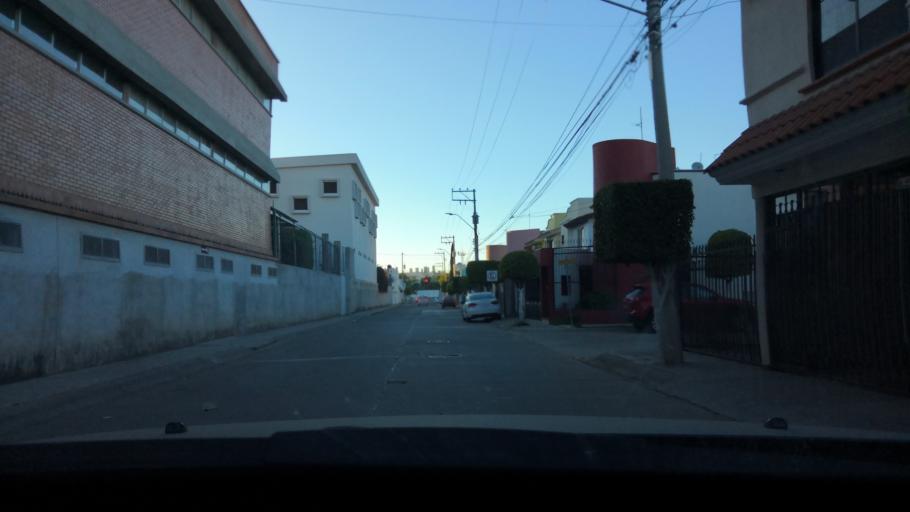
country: MX
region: Guanajuato
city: Leon
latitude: 21.1648
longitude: -101.6607
